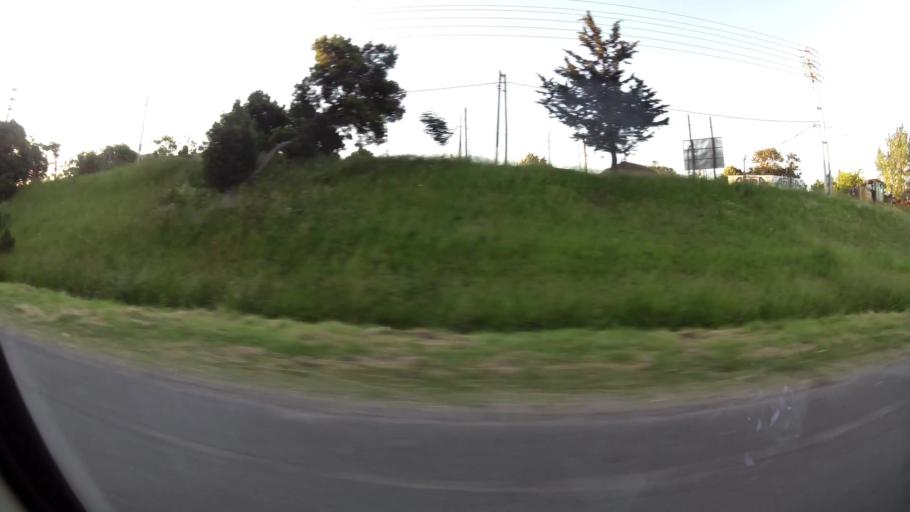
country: AR
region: Buenos Aires
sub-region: Partido de Quilmes
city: Quilmes
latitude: -34.8135
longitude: -58.1796
